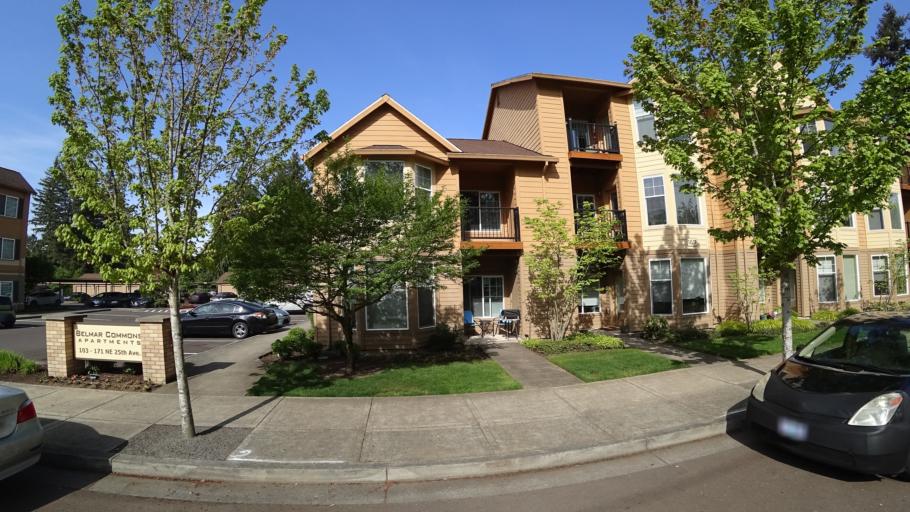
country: US
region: Oregon
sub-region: Washington County
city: Hillsboro
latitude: 45.5219
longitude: -122.9565
